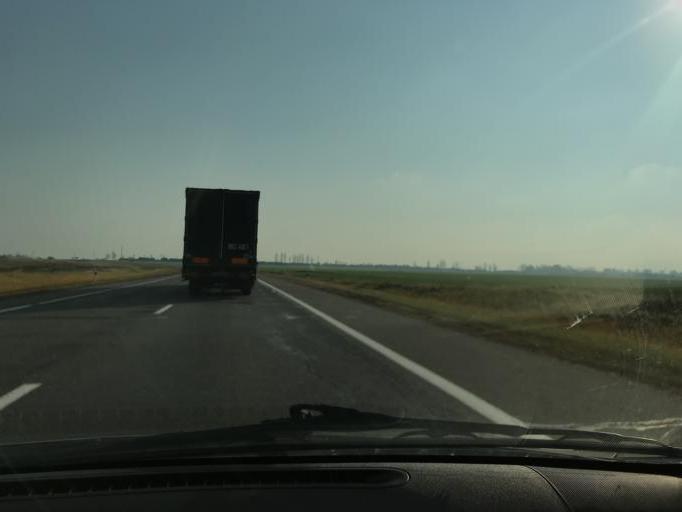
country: BY
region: Vitebsk
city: Chashniki
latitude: 55.0087
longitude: 29.1308
